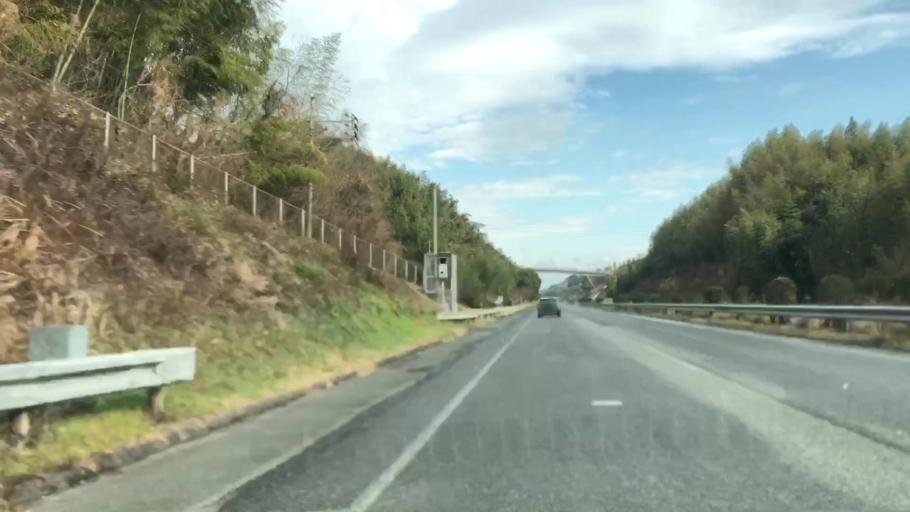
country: JP
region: Saga Prefecture
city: Tosu
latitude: 33.3649
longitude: 130.4486
